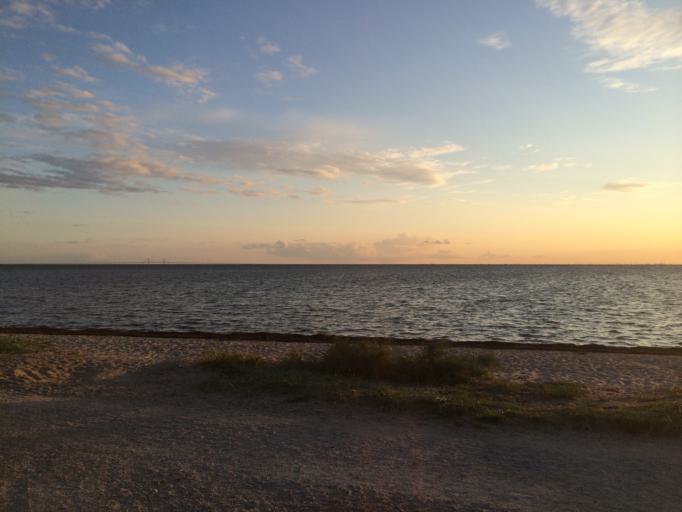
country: SE
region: Skane
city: Bjarred
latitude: 55.7234
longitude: 13.0046
